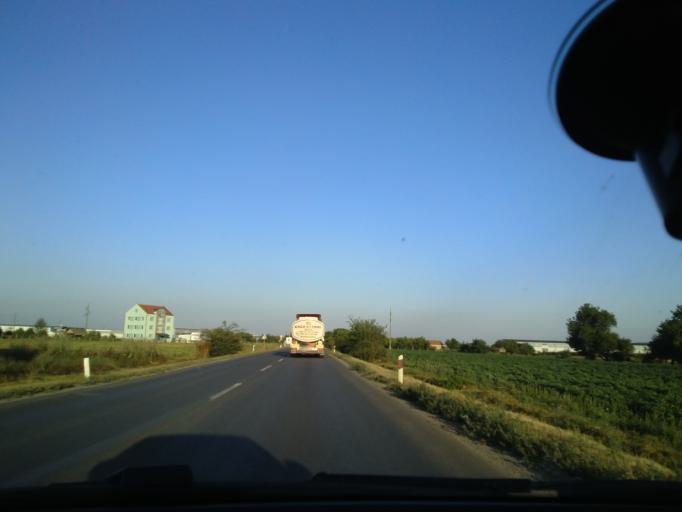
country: RS
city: Rumenka
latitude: 45.2856
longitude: 19.7623
